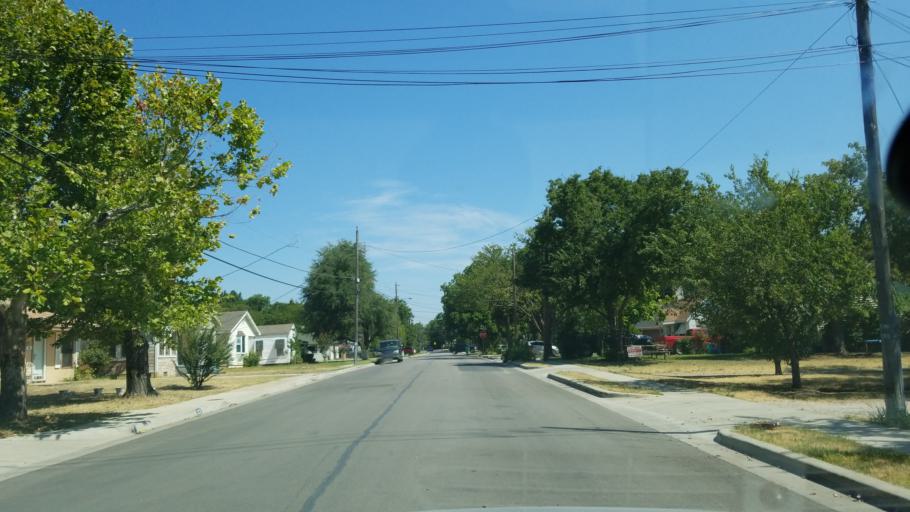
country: US
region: Texas
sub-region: Dallas County
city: Cockrell Hill
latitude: 32.7402
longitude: -96.8872
